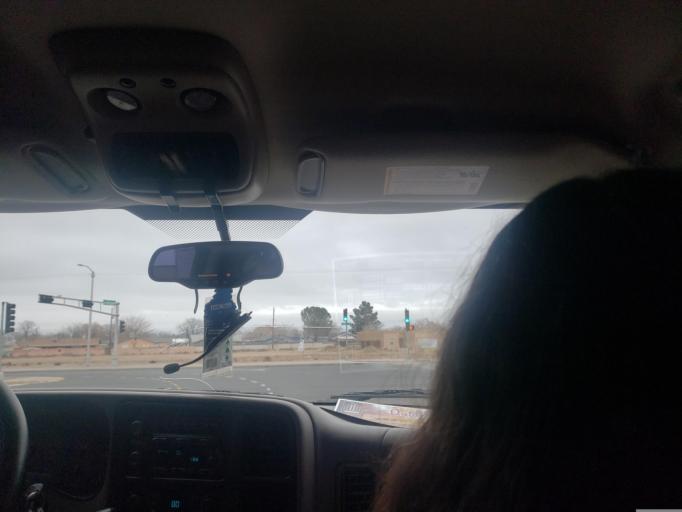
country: US
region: New Mexico
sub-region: Bernalillo County
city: Albuquerque
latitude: 35.0923
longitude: -106.7114
